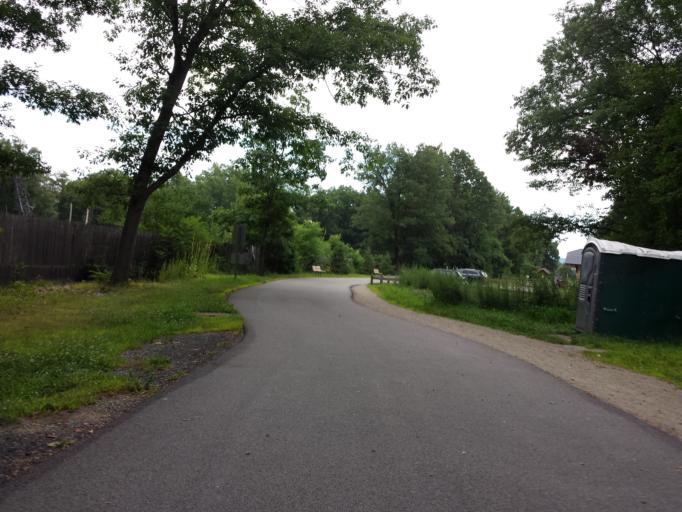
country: US
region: New York
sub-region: Dutchess County
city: Hillside Lake
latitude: 41.5858
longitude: -73.8076
